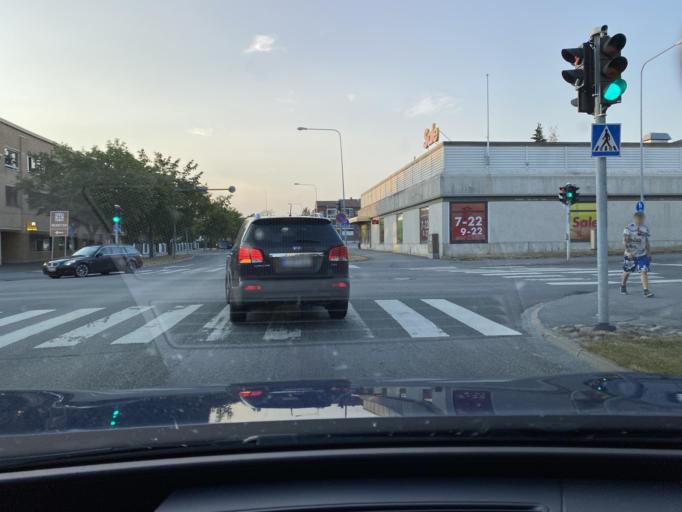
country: FI
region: Central Ostrobothnia
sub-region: Kokkola
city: Kokkola
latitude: 63.8386
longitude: 23.1378
